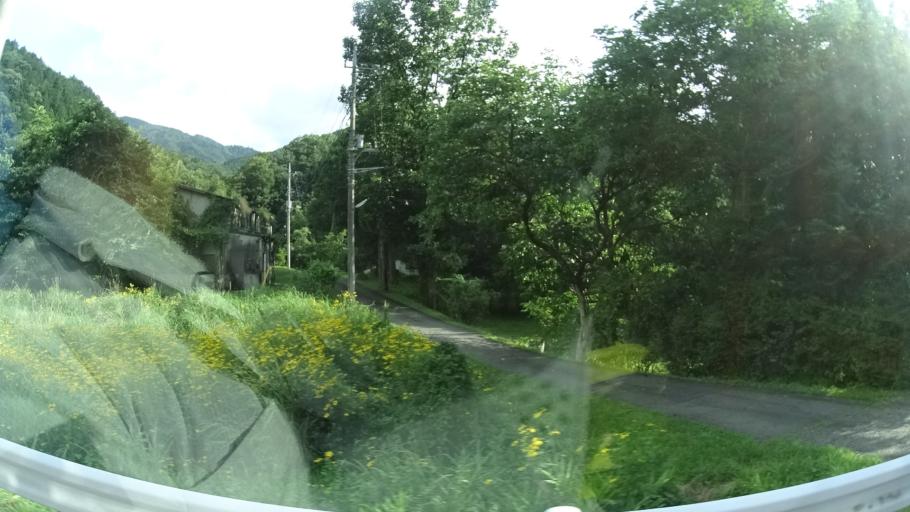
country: JP
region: Tochigi
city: Nikko
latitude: 36.6655
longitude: 139.4701
